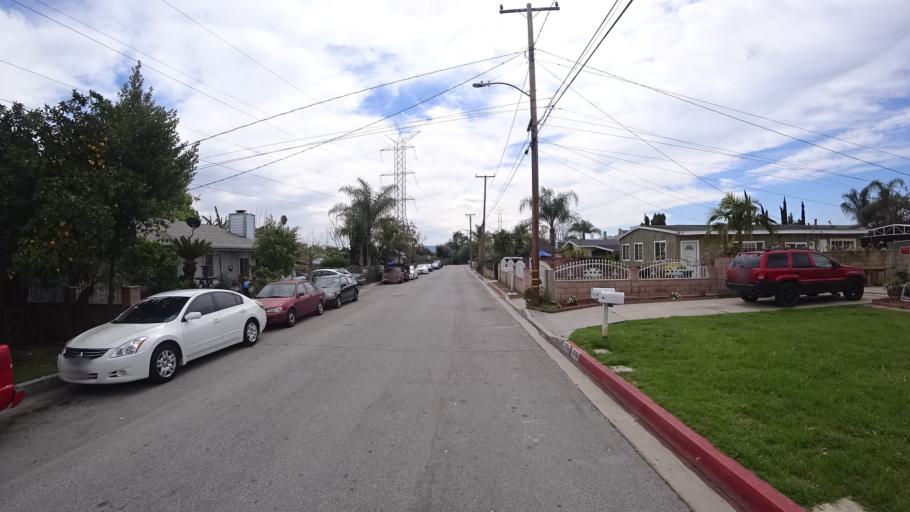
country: US
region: California
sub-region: Los Angeles County
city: Baldwin Park
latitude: 34.0778
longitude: -117.9908
